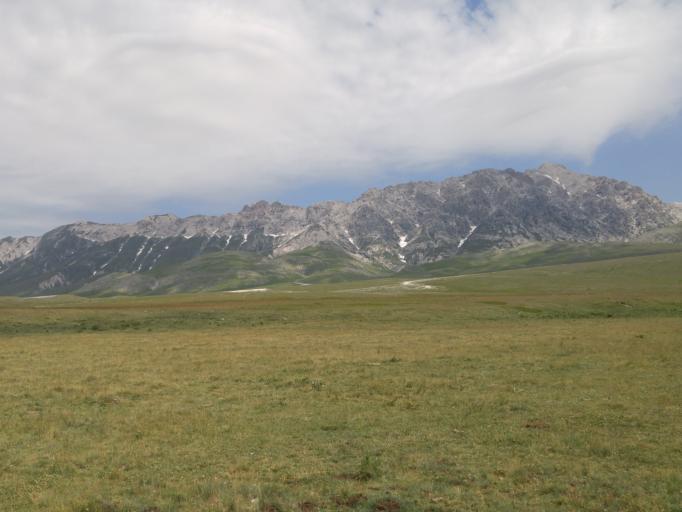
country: IT
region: Abruzzo
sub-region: Provincia dell' Aquila
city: Santo Stefano di Sessanio
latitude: 42.3988
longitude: 13.6641
